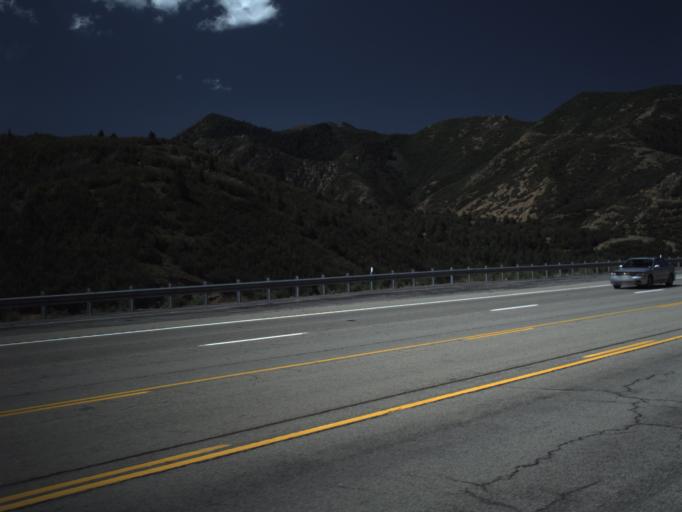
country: US
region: Utah
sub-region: Utah County
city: Mapleton
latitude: 40.0294
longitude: -111.5081
